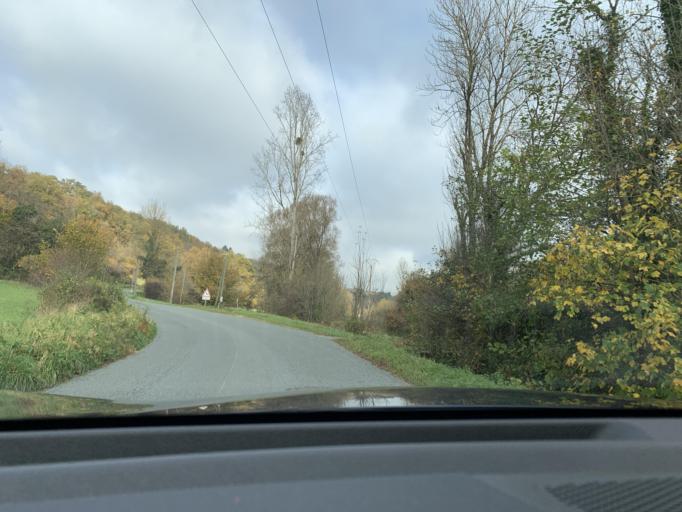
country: FR
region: Rhone-Alpes
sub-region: Departement du Rhone
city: Charnay
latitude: 45.8814
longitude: 4.6467
